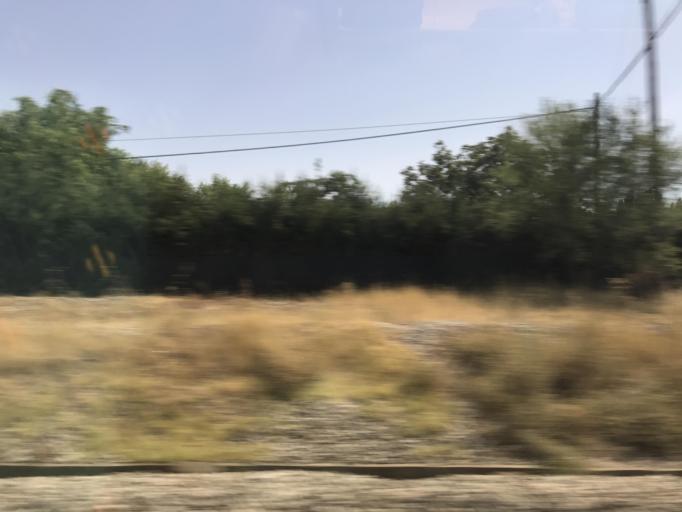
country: ES
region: Castille and Leon
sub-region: Provincia de Valladolid
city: Cabezon
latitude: 41.7318
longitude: -4.6551
